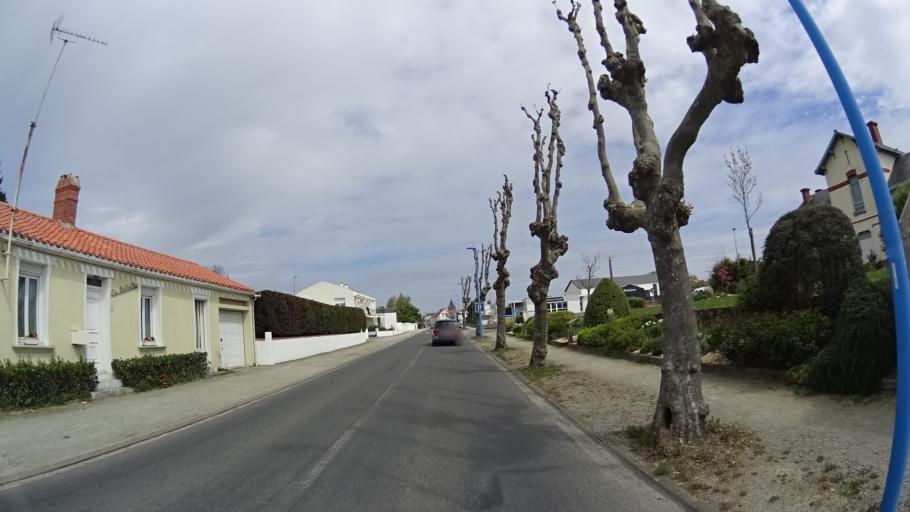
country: FR
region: Pays de la Loire
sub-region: Departement de la Vendee
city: Beauvoir-sur-Mer
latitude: 46.9111
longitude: -2.0466
